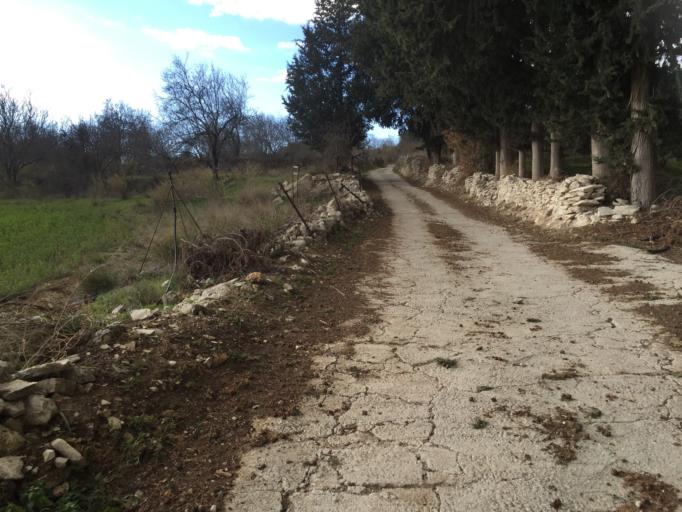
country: CY
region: Pafos
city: Mesogi
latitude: 34.8464
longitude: 32.5050
